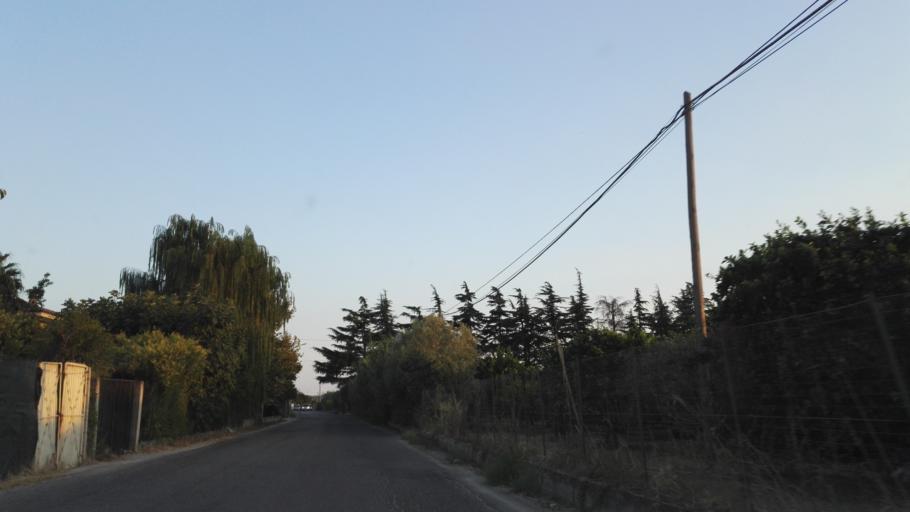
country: IT
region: Calabria
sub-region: Provincia di Reggio Calabria
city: Caulonia Marina
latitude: 38.3589
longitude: 16.4696
